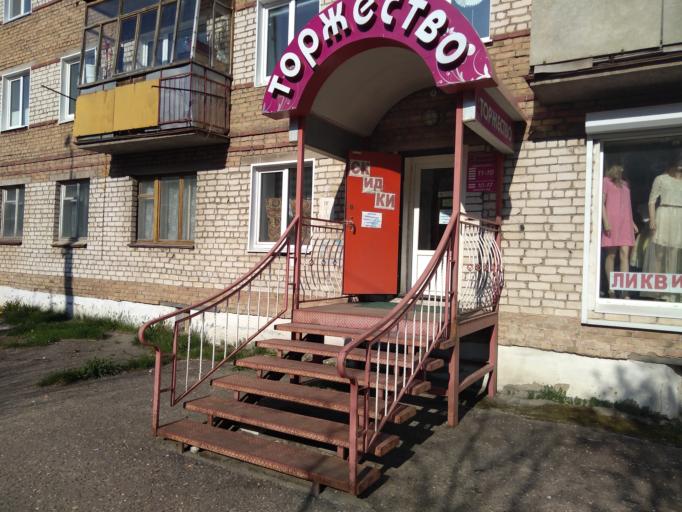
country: RU
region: Komi Republic
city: Pechora
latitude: 65.1245
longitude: 57.1543
